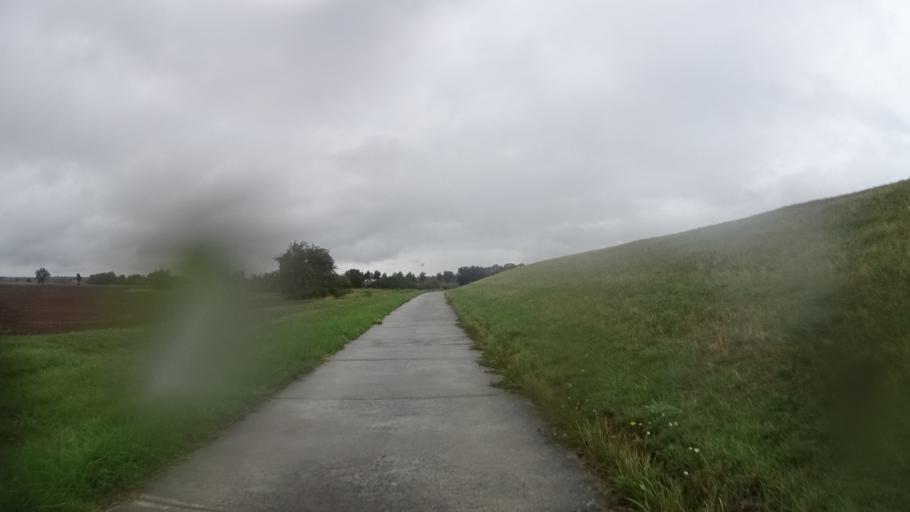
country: DE
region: Lower Saxony
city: Damnatz
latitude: 53.1605
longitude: 11.1144
